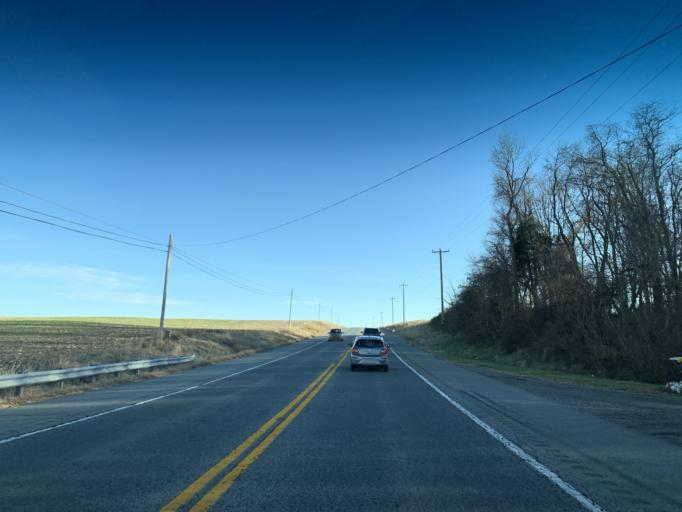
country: US
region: Delaware
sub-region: New Castle County
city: Middletown
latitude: 39.4443
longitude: -75.8672
